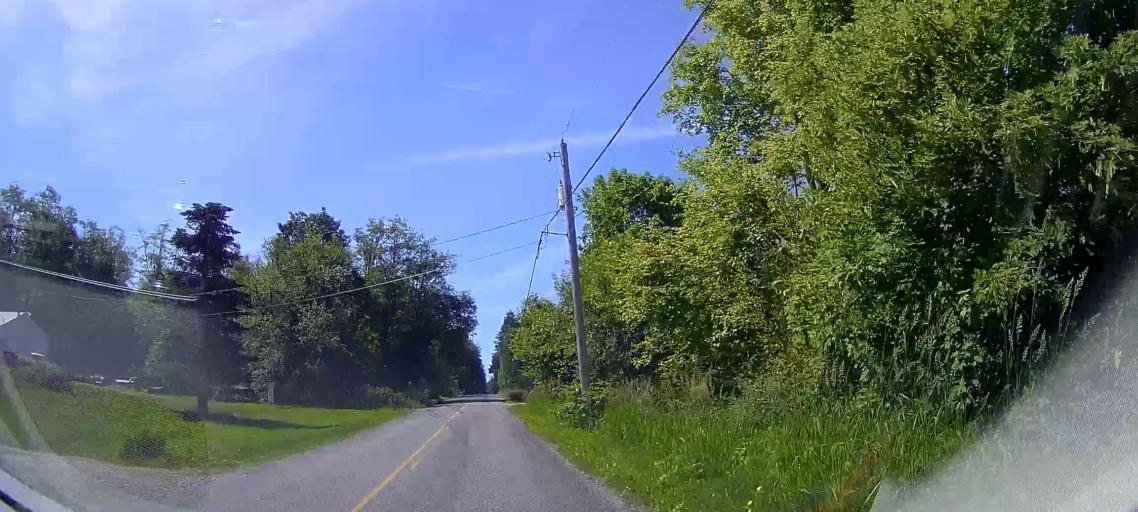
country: US
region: Washington
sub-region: Skagit County
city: Sedro-Woolley
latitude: 48.5563
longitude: -122.2466
